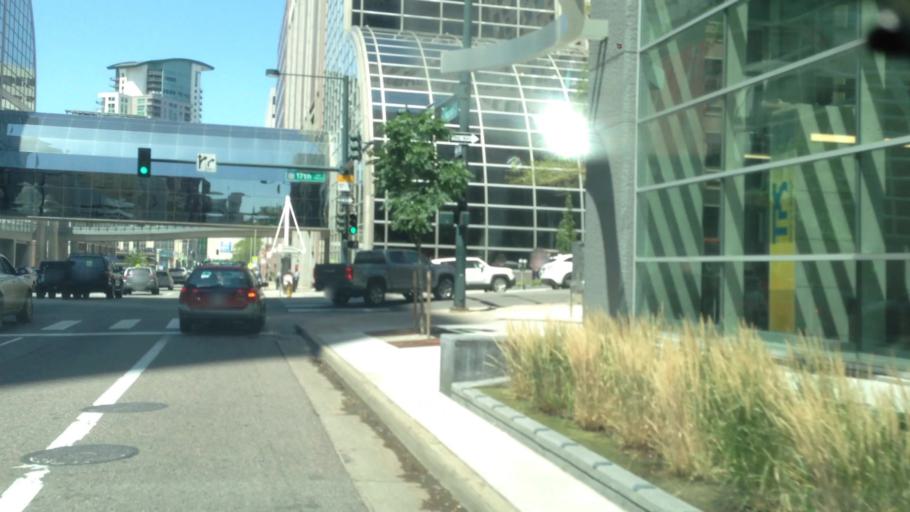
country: US
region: Colorado
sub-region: Denver County
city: Denver
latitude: 39.7430
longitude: -104.9860
